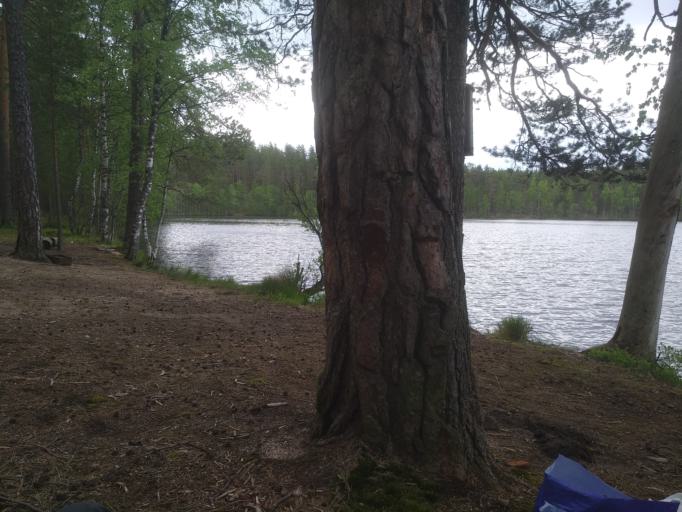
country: RU
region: Leningrad
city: Michurinskoye
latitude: 60.5978
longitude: 29.9191
